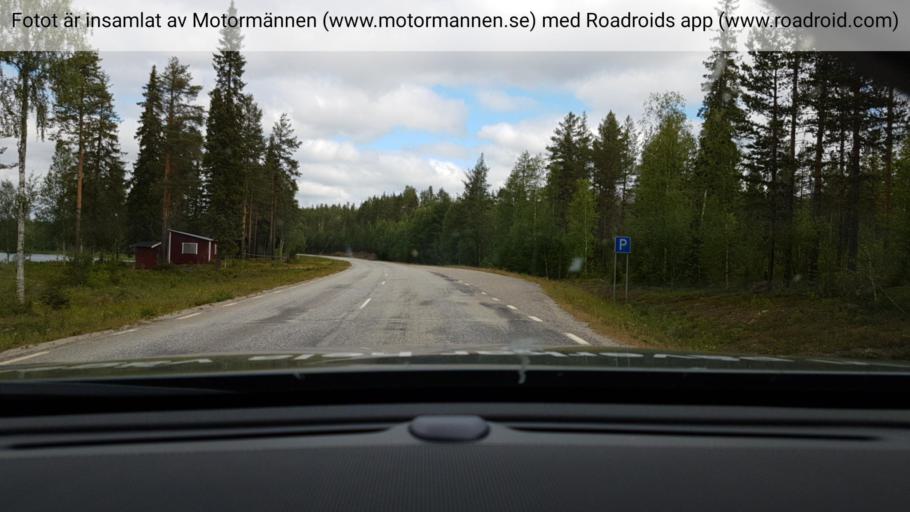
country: SE
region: Vaesterbotten
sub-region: Mala Kommun
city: Mala
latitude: 64.9391
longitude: 18.6248
